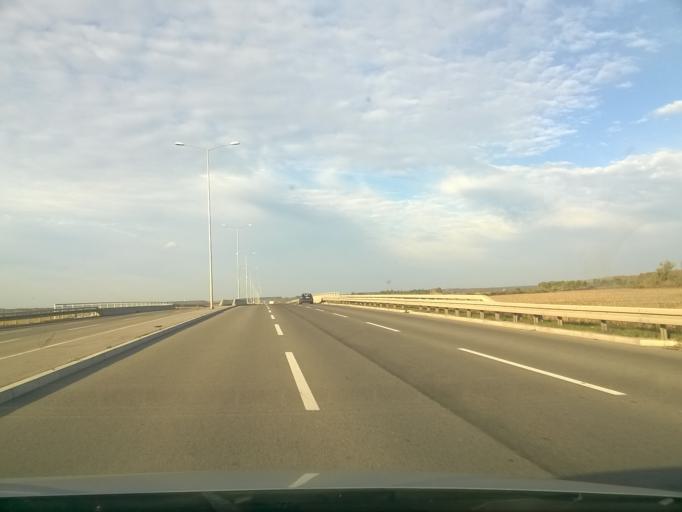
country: RS
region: Central Serbia
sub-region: Belgrade
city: Zemun
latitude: 44.9006
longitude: 20.4334
